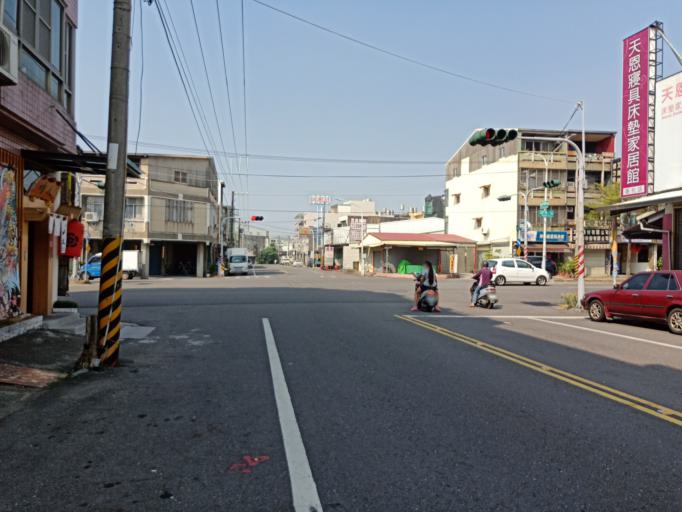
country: TW
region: Taiwan
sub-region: Tainan
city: Tainan
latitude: 23.1311
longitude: 120.2971
